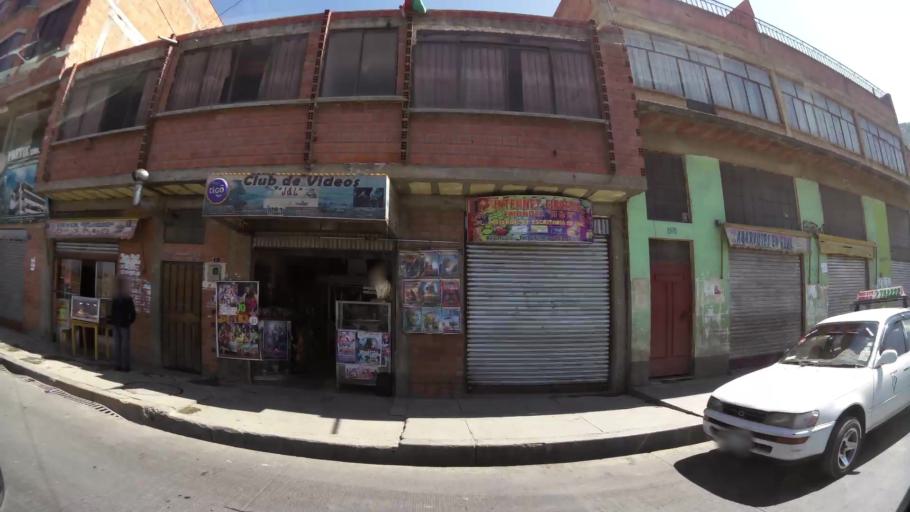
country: BO
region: La Paz
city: La Paz
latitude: -16.5332
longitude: -68.1405
